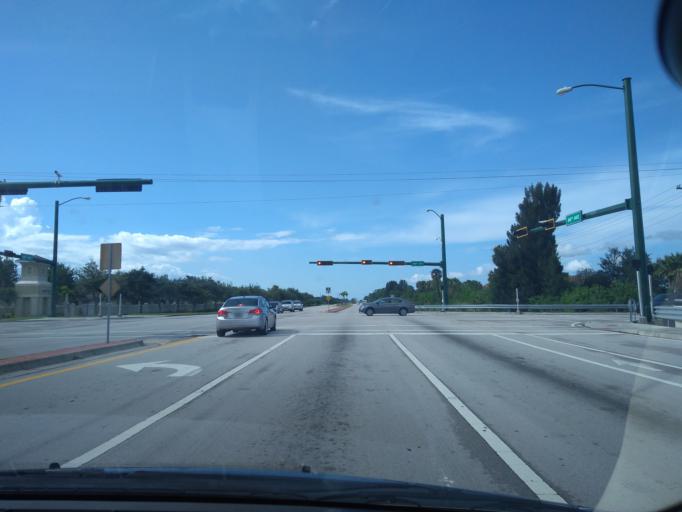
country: US
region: Florida
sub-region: Indian River County
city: West Vero Corridor
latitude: 27.6460
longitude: -80.4631
